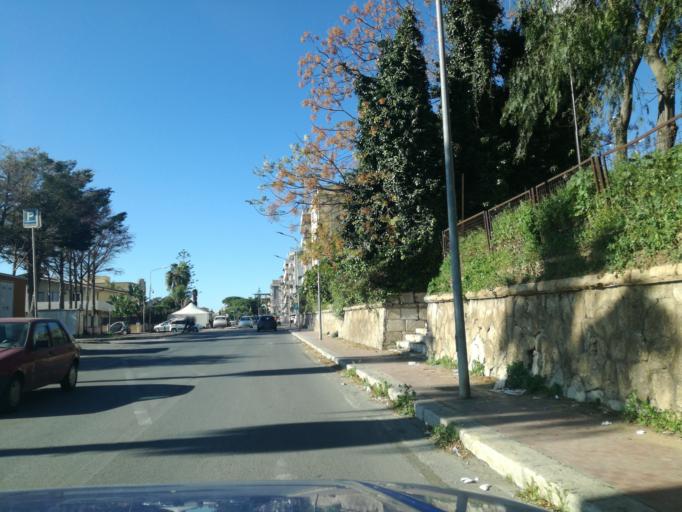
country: IT
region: Sicily
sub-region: Provincia di Caltanissetta
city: Gela
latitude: 37.0721
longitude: 14.2296
